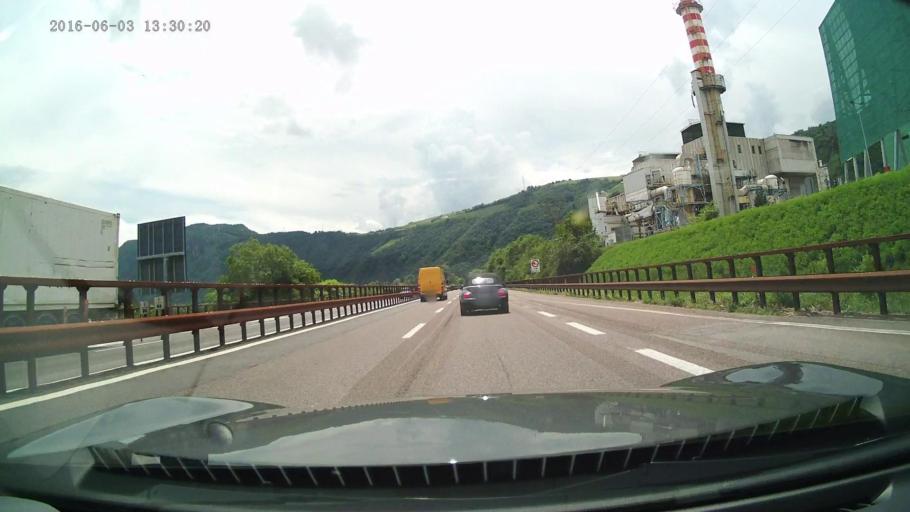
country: IT
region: Trentino-Alto Adige
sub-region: Bolzano
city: San Giacomo
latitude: 46.4675
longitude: 11.3090
